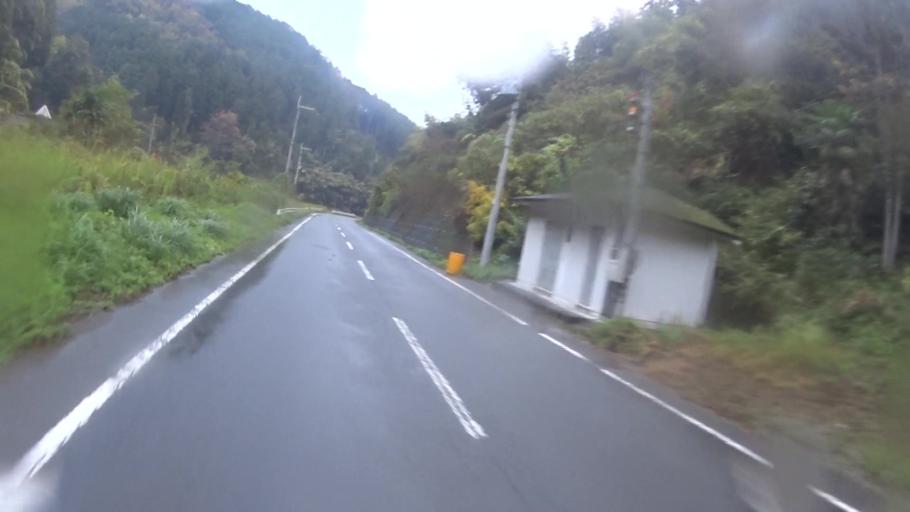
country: JP
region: Kyoto
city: Miyazu
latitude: 35.4613
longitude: 135.2361
